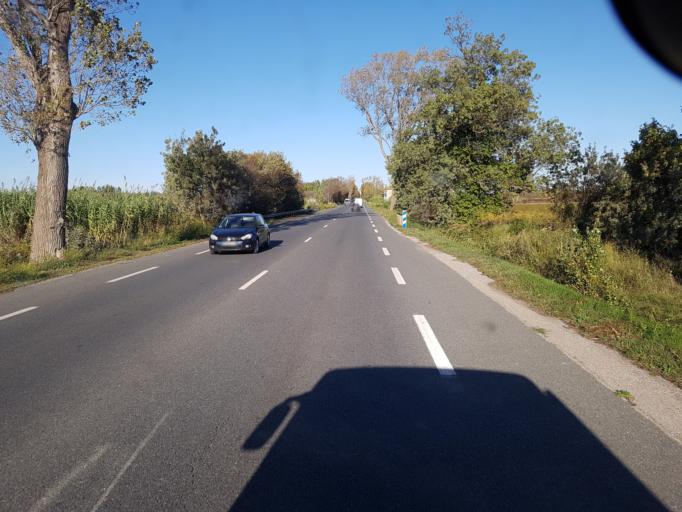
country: FR
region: Languedoc-Roussillon
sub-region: Departement de l'Aude
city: Coursan
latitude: 43.2118
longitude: 3.0301
